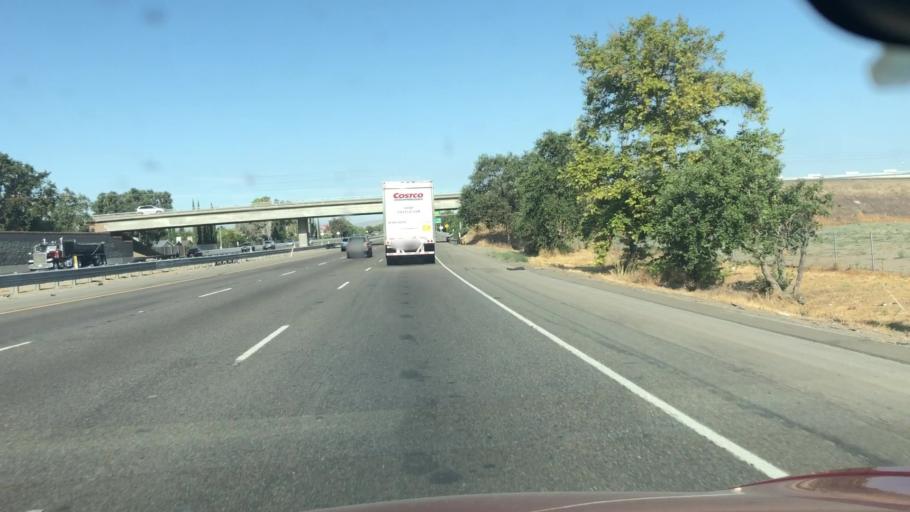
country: US
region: California
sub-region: San Joaquin County
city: Tracy
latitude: 37.7631
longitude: -121.4245
